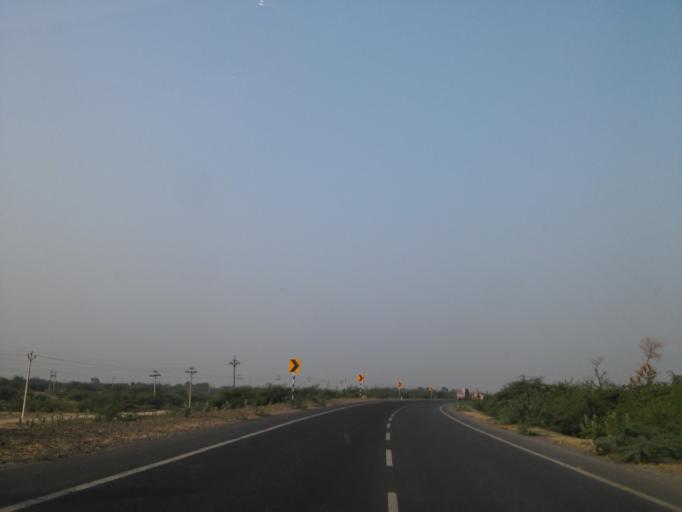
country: IN
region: Gujarat
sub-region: Kachchh
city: Bhachau
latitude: 23.3120
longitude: 70.1260
